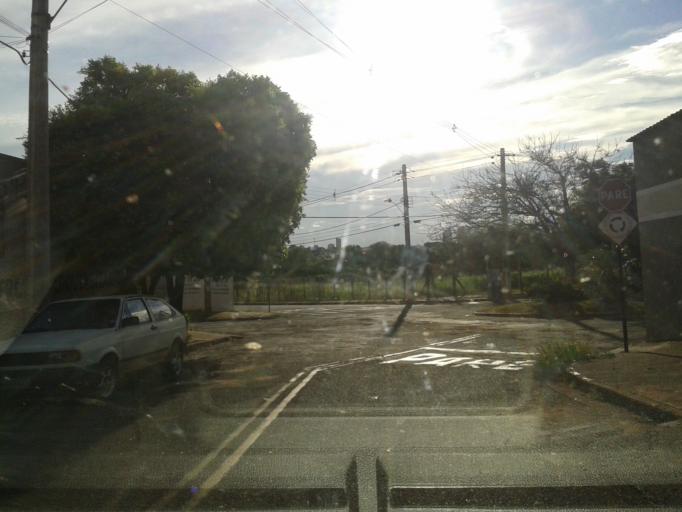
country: BR
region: Minas Gerais
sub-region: Ituiutaba
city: Ituiutaba
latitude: -18.9738
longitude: -49.4443
